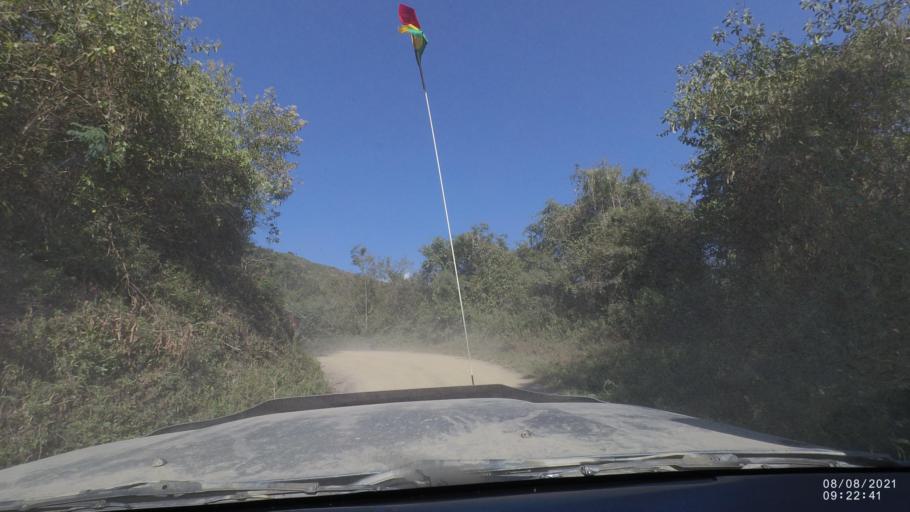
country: BO
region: La Paz
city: Quime
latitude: -16.5762
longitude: -66.7169
